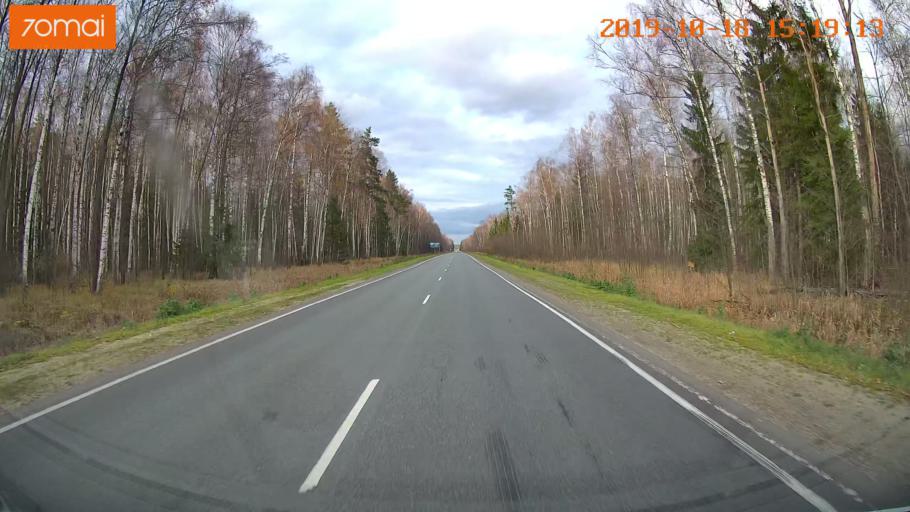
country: RU
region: Vladimir
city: Anopino
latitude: 55.6697
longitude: 40.7360
